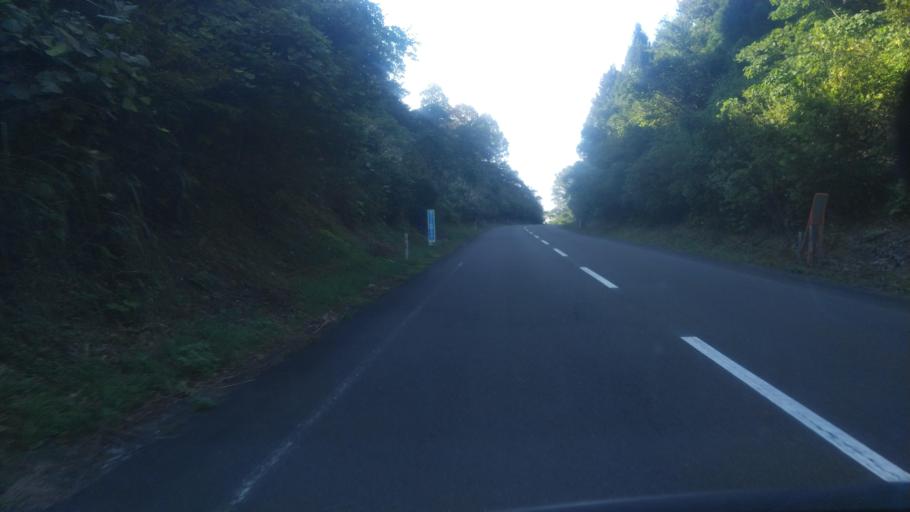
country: JP
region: Miyagi
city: Okawara
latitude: 38.1001
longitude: 140.6972
